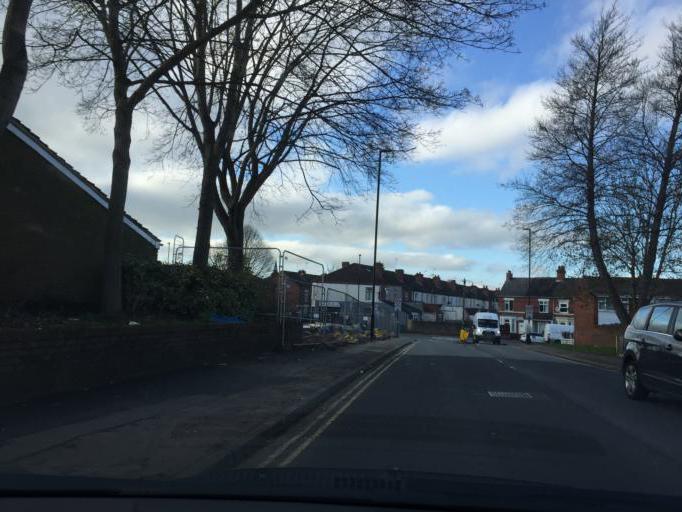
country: GB
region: England
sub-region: Coventry
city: Coventry
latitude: 52.4149
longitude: -1.4995
